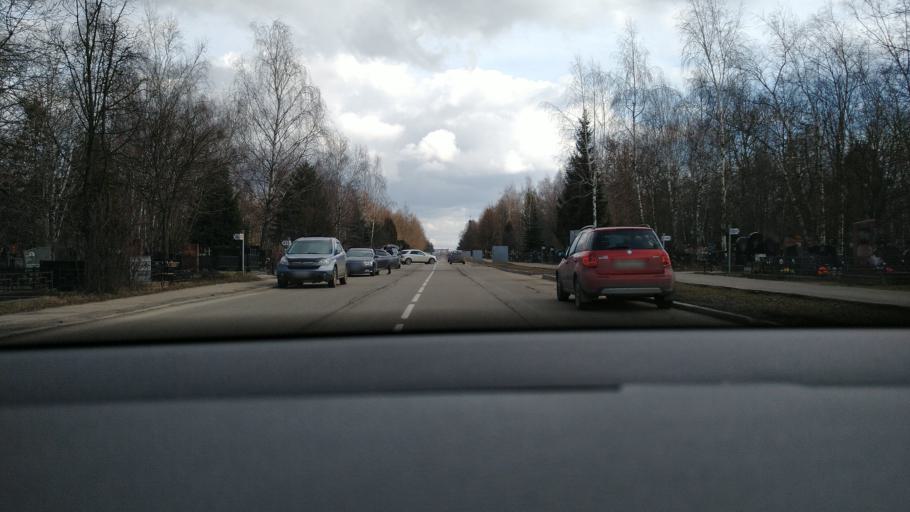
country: RU
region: Moskovskaya
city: Mosrentgen
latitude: 55.6066
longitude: 37.4372
